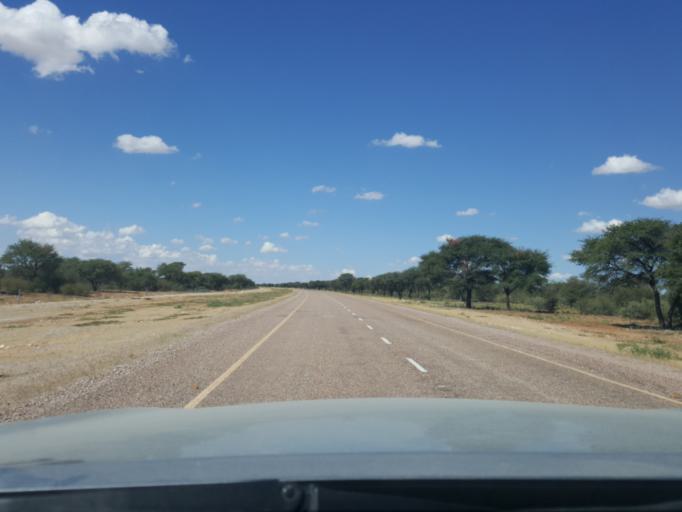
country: BW
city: Lehututu
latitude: -23.9227
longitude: 22.0096
